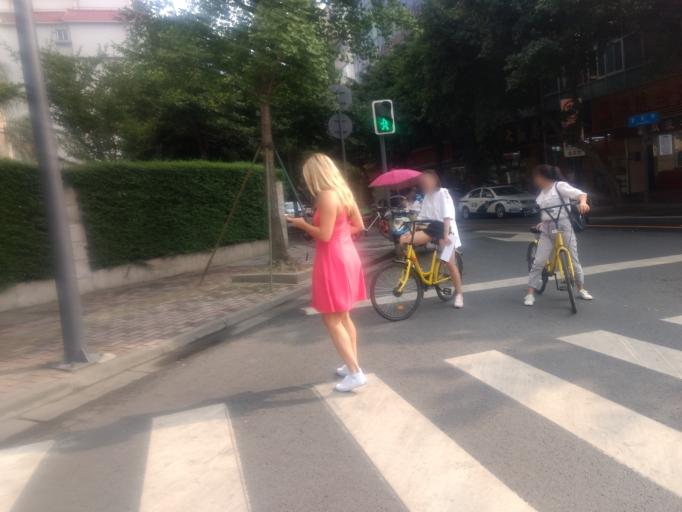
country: CN
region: Sichuan
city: Chengdu
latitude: 30.6739
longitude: 104.0683
